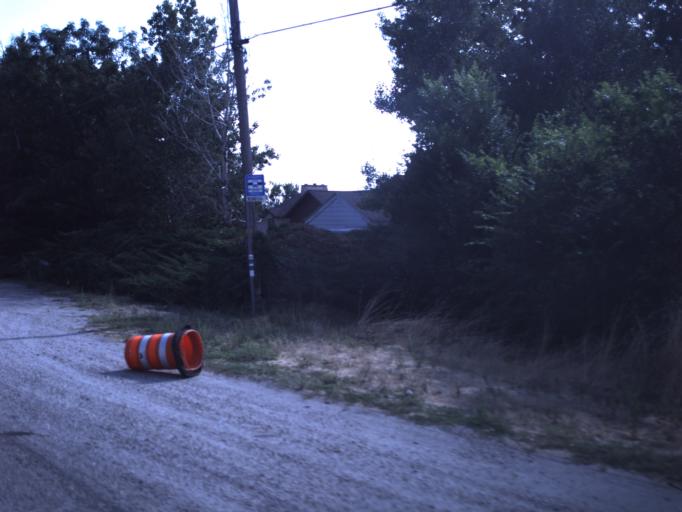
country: US
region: Utah
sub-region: Box Elder County
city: Willard
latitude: 41.3955
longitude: -112.0344
